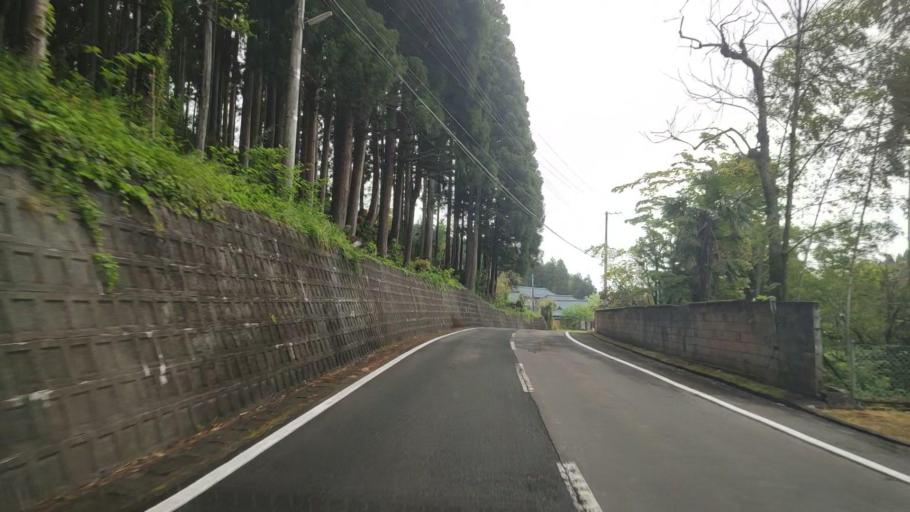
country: JP
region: Niigata
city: Gosen
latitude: 37.7222
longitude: 139.1280
